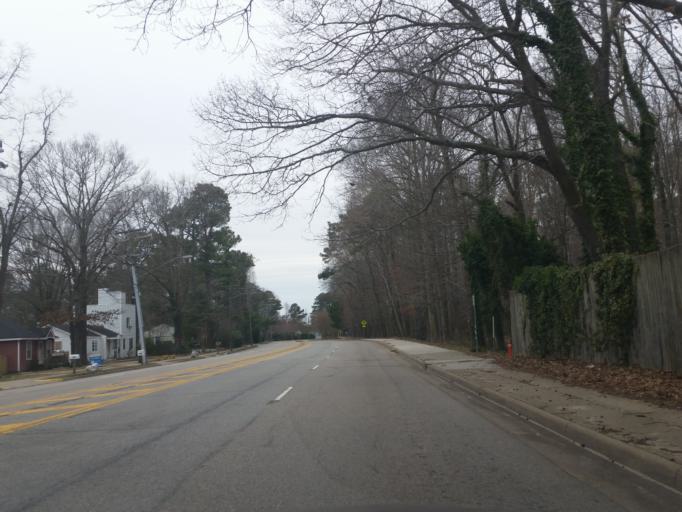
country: US
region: Virginia
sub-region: City of Virginia Beach
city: Virginia Beach
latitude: 36.8259
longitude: -75.9764
